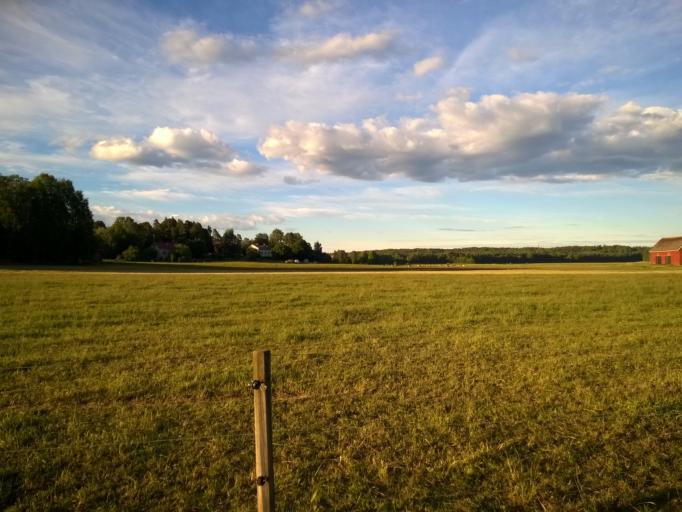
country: FI
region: Uusimaa
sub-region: Helsinki
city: Vantaa
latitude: 60.2188
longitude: 25.0122
